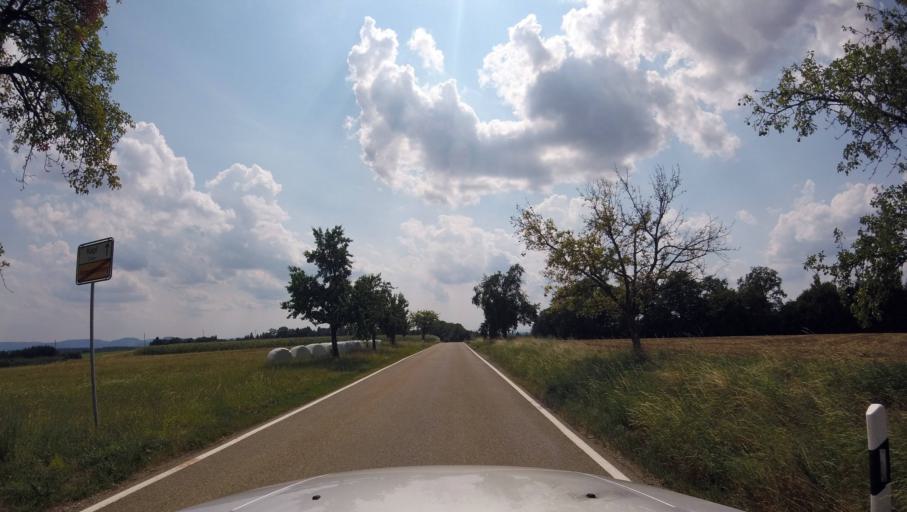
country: DE
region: Baden-Wuerttemberg
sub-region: Regierungsbezirk Stuttgart
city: Spraitbach
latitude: 48.8812
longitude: 9.7281
